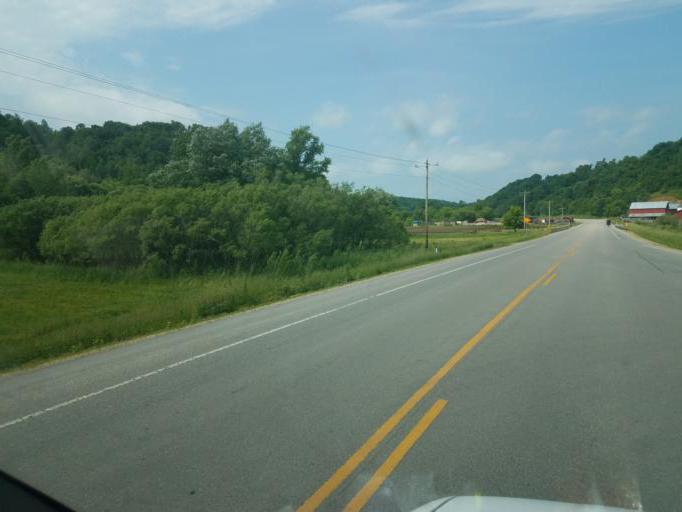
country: US
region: Wisconsin
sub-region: Monroe County
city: Cashton
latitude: 43.7340
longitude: -90.7069
